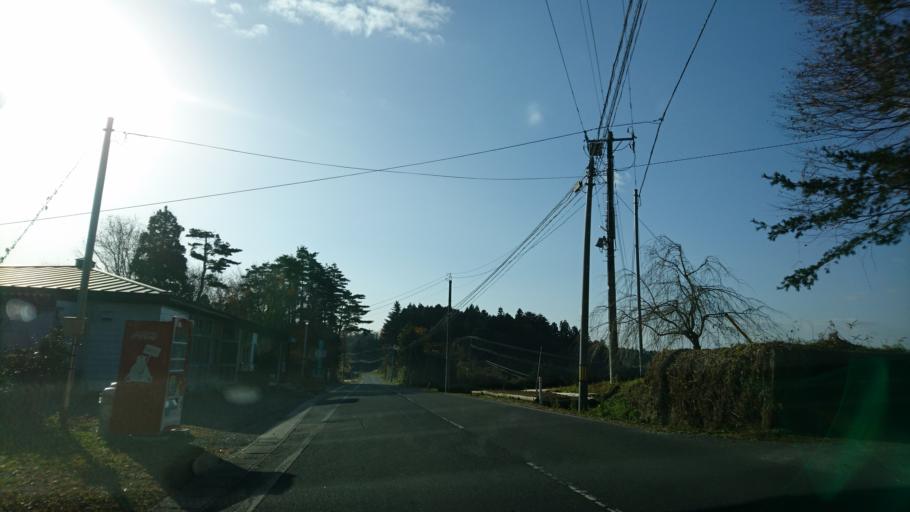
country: JP
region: Iwate
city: Ichinoseki
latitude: 38.8799
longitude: 141.2914
